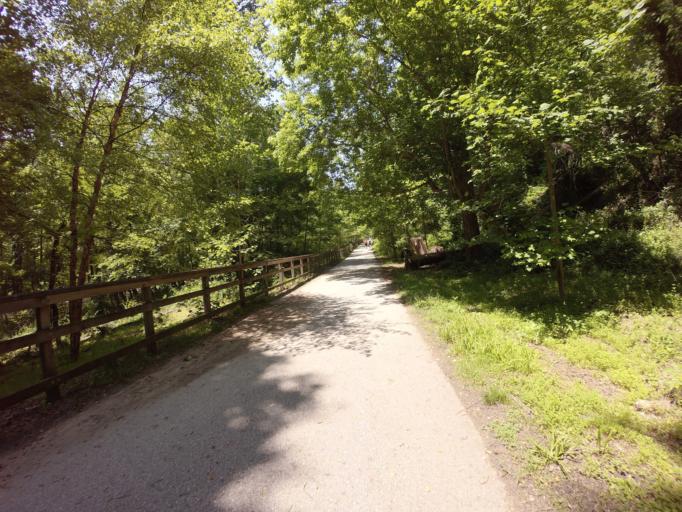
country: US
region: Maryland
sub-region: Howard County
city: Ilchester
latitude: 39.2478
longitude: -76.7581
